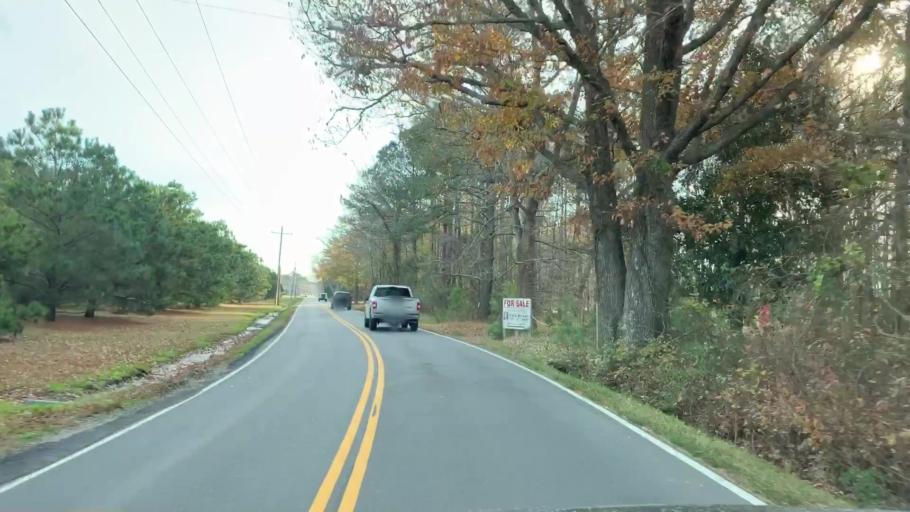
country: US
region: Virginia
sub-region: City of Virginia Beach
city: Virginia Beach
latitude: 36.7235
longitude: -76.0654
